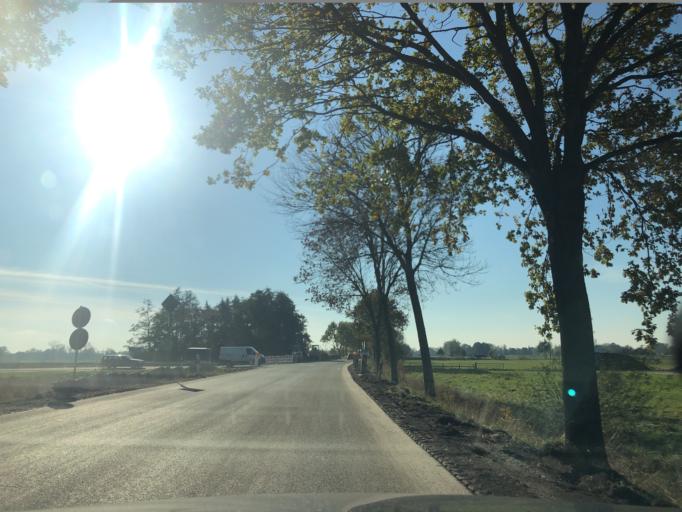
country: DE
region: Lower Saxony
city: Lemwerder
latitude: 53.1582
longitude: 8.5583
